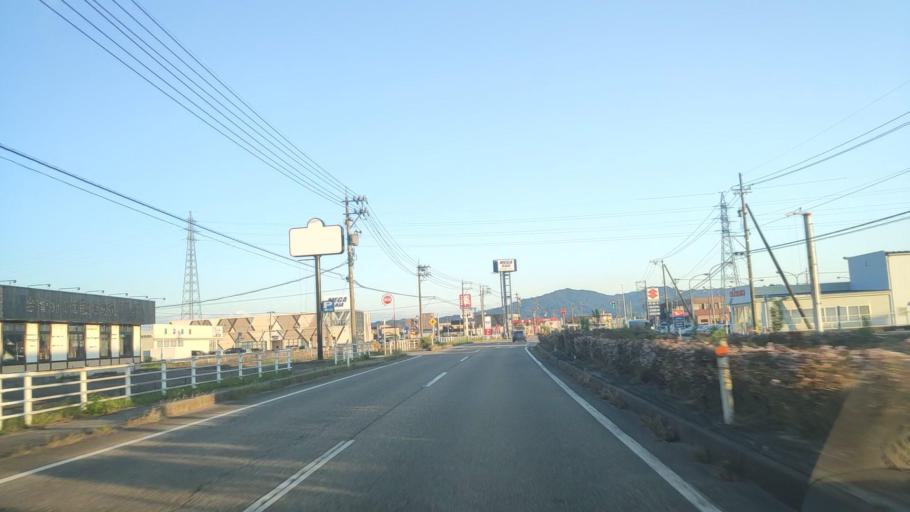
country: JP
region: Toyama
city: Himi
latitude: 36.8364
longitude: 136.9892
